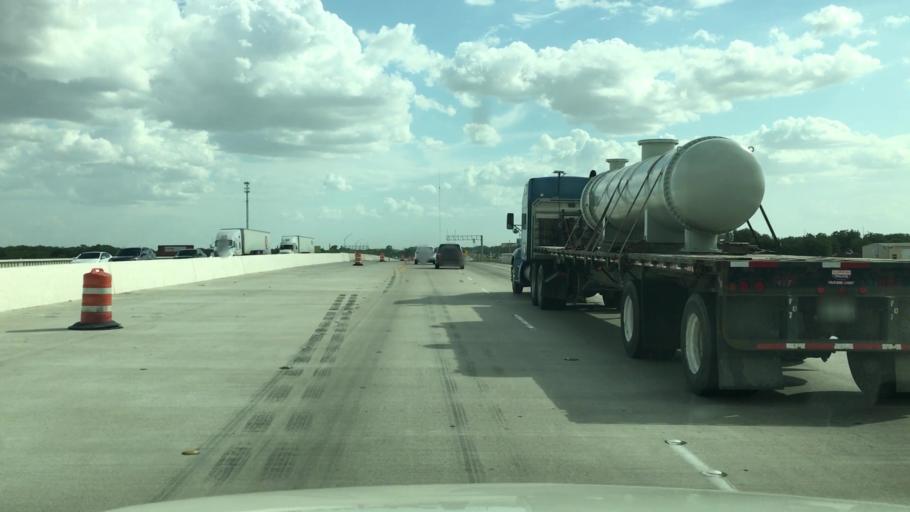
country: US
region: Texas
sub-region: McLennan County
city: Bruceville-Eddy
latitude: 31.3077
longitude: -97.2446
